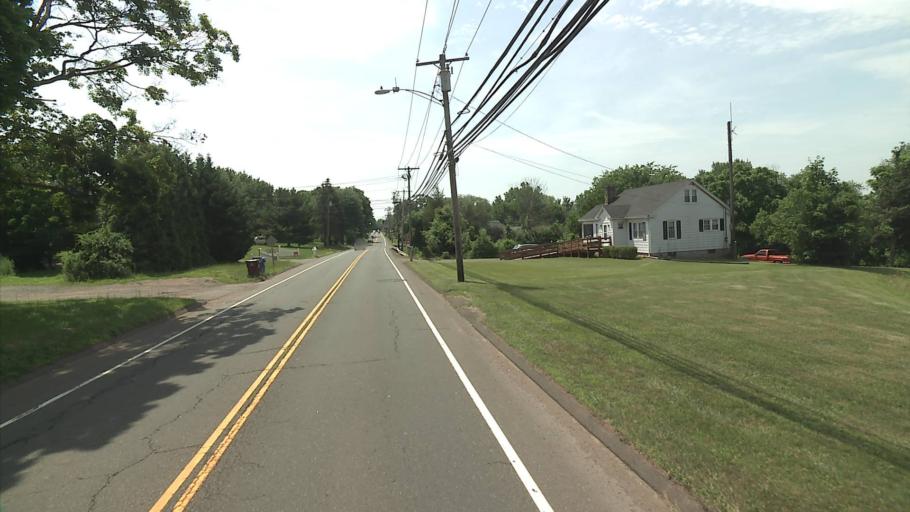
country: US
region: Connecticut
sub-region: New Haven County
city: North Branford
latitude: 41.3207
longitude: -72.7711
